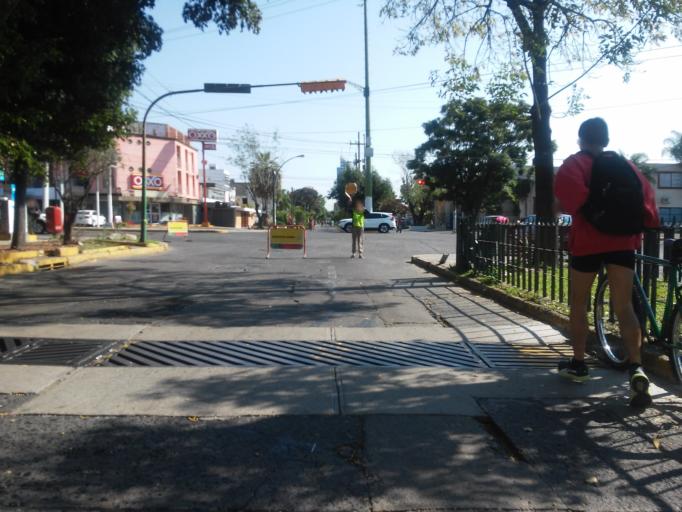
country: MX
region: Jalisco
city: Guadalajara
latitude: 20.6613
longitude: -103.4075
